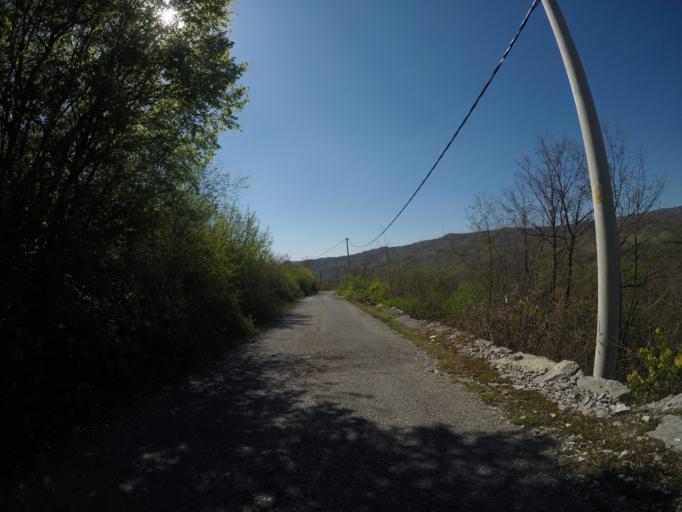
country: ME
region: Danilovgrad
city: Danilovgrad
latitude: 42.5241
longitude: 19.0475
